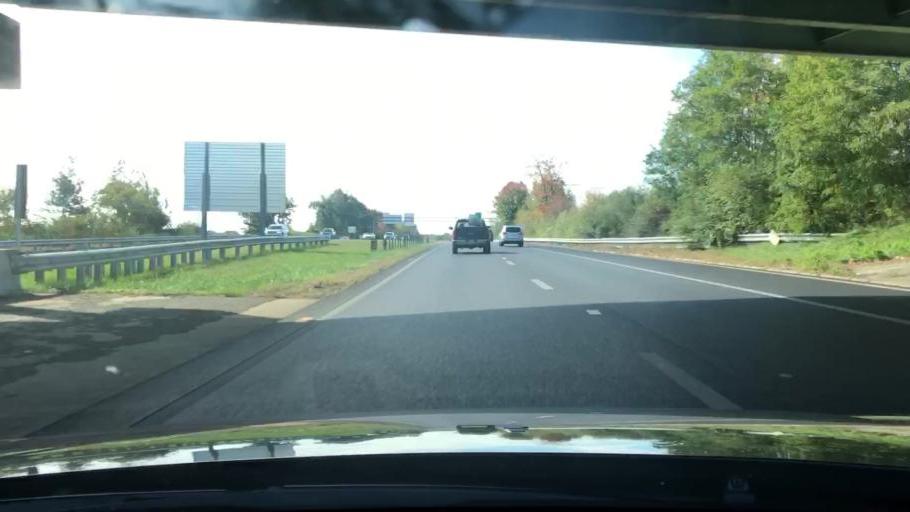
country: US
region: Massachusetts
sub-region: Essex County
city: Methuen
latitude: 42.7464
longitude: -71.1569
